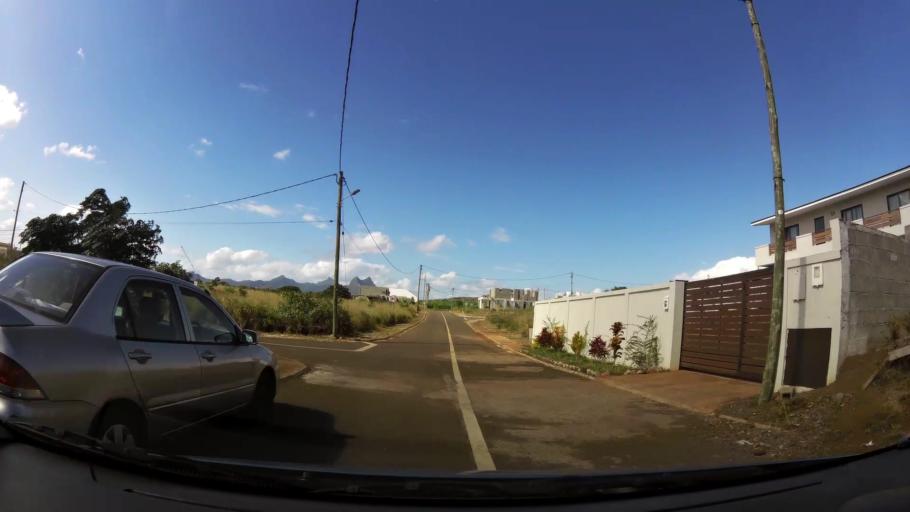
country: MU
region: Black River
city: Albion
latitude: -20.2235
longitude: 57.4172
